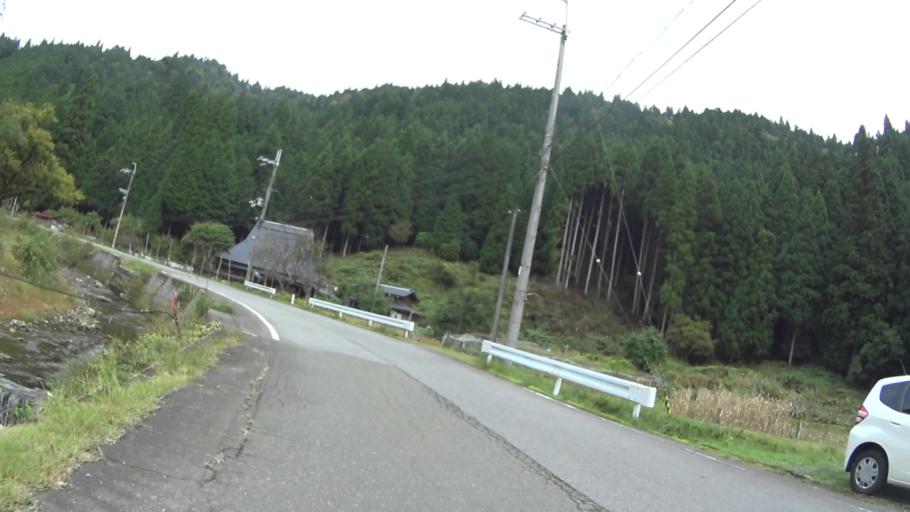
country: JP
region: Shiga Prefecture
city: Kitahama
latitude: 35.2605
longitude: 135.7525
